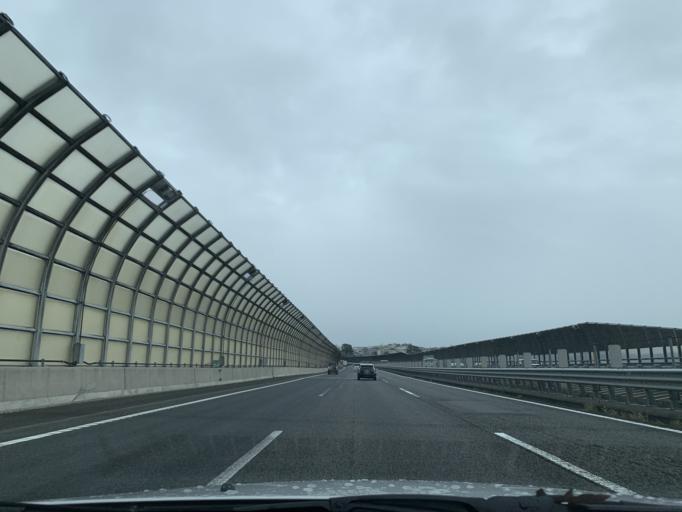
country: JP
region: Kanagawa
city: Hadano
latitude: 35.3591
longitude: 139.2469
